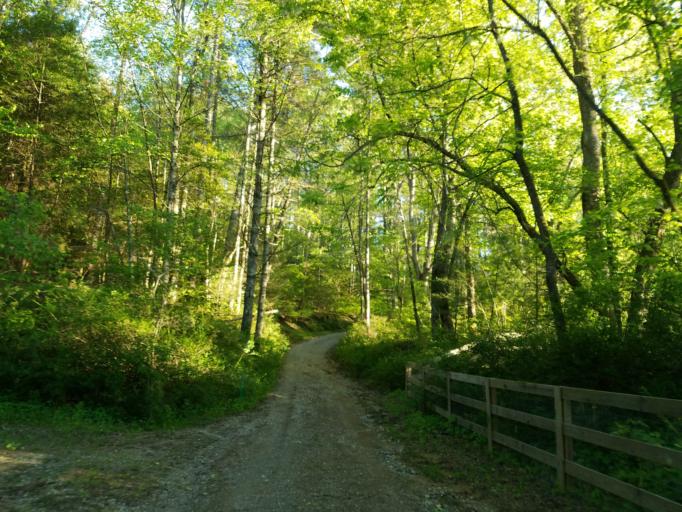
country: US
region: Georgia
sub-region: Union County
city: Blairsville
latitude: 34.7362
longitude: -84.0597
